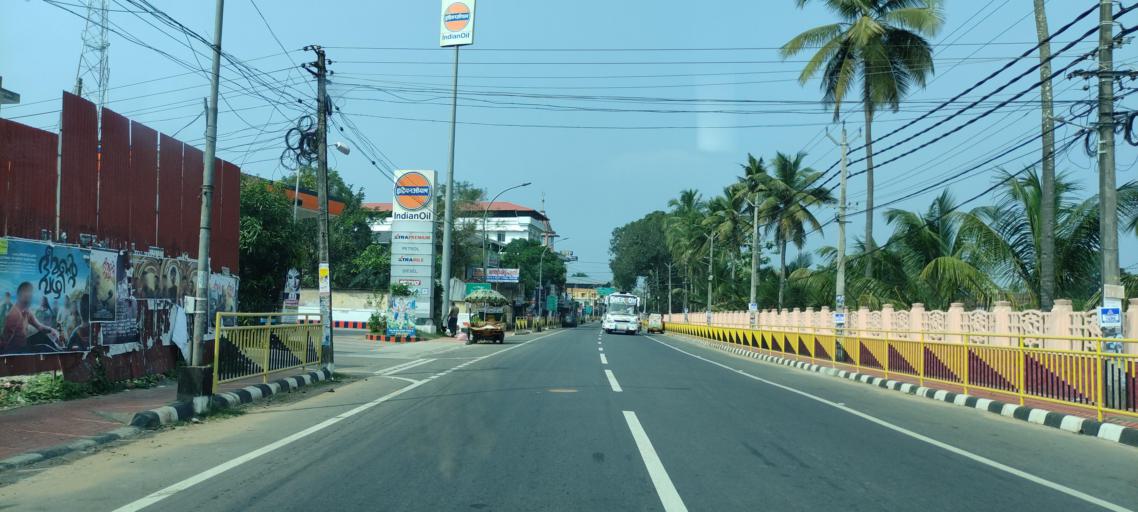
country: IN
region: Kerala
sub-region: Pattanamtitta
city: Adur
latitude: 9.2208
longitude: 76.6790
